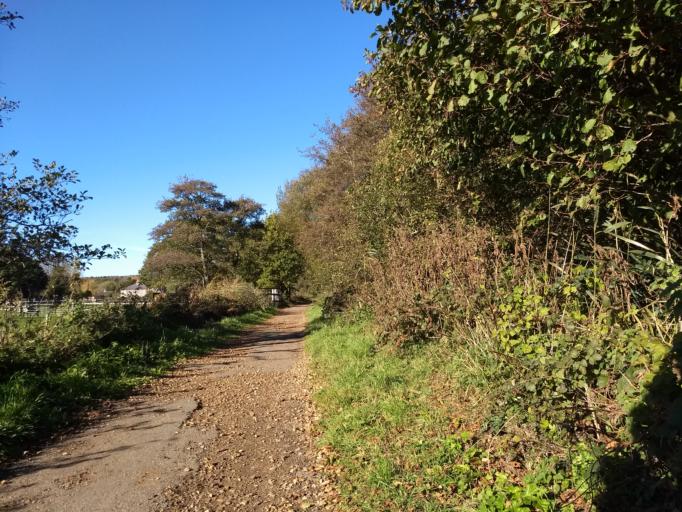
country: GB
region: England
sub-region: Isle of Wight
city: Newport
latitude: 50.6708
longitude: -1.2821
